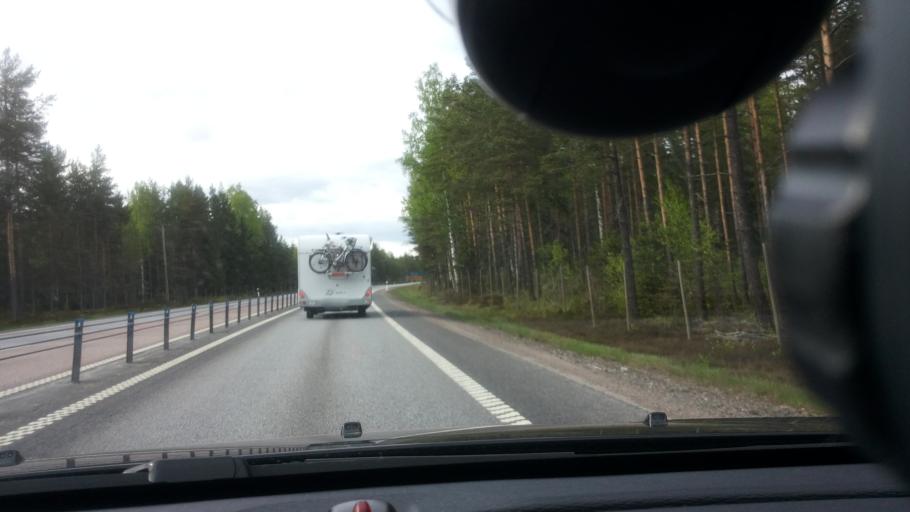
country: SE
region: Gaevleborg
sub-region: Gavle Kommun
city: Norrsundet
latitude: 61.0181
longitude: 16.9778
